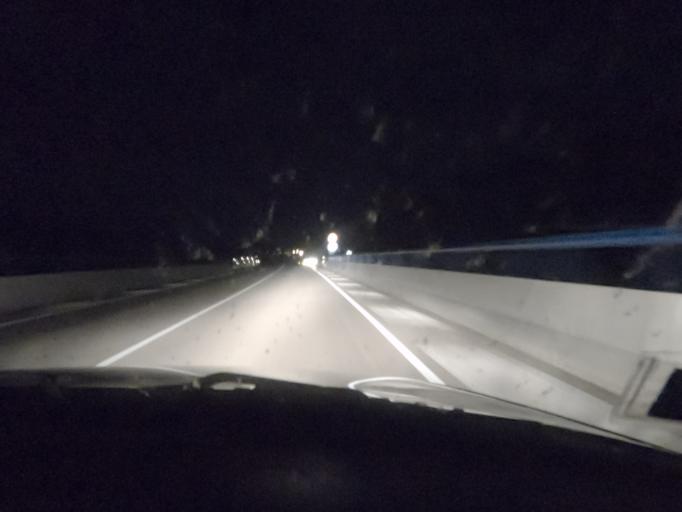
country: ES
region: Castille and Leon
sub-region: Provincia de Salamanca
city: Herguijuela de Ciudad Rodrigo
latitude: 40.4930
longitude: -6.5800
